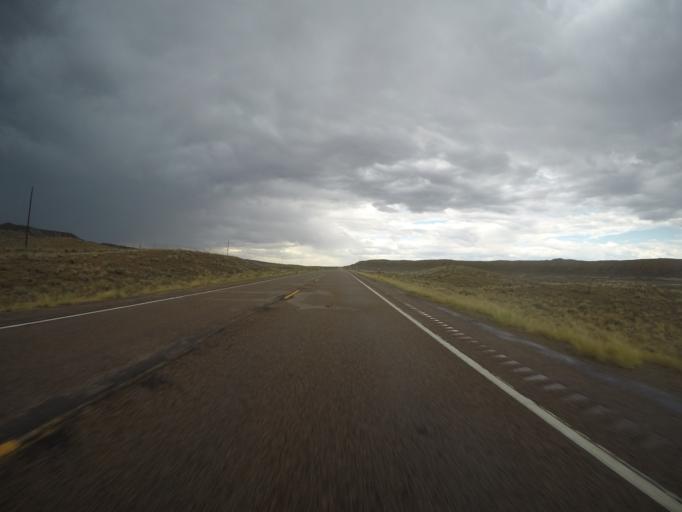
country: US
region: Colorado
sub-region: Rio Blanco County
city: Rangely
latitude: 40.2515
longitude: -108.8451
